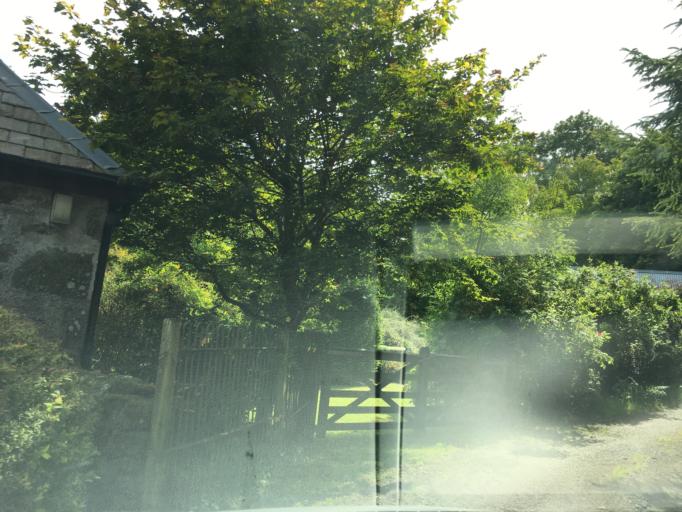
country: GB
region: Scotland
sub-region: Argyll and Bute
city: Oban
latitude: 56.2472
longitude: -5.6244
